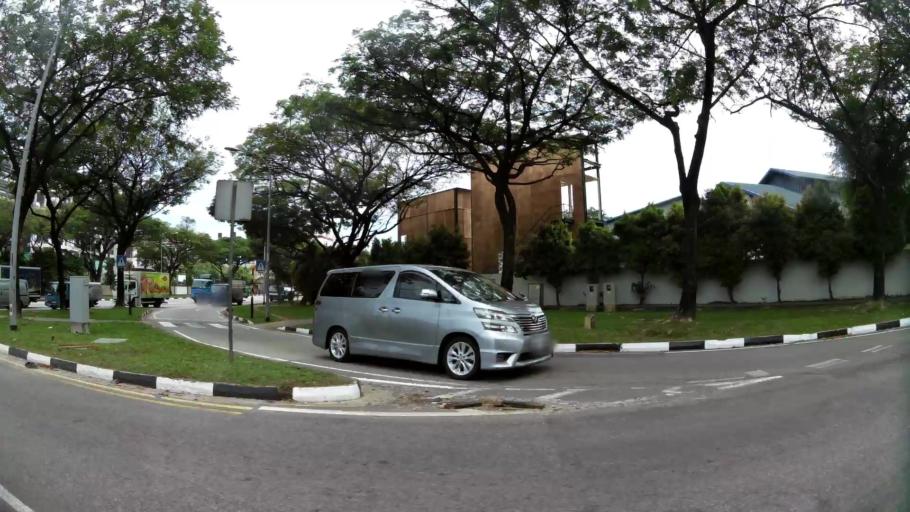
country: SG
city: Singapore
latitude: 1.3144
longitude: 103.7199
